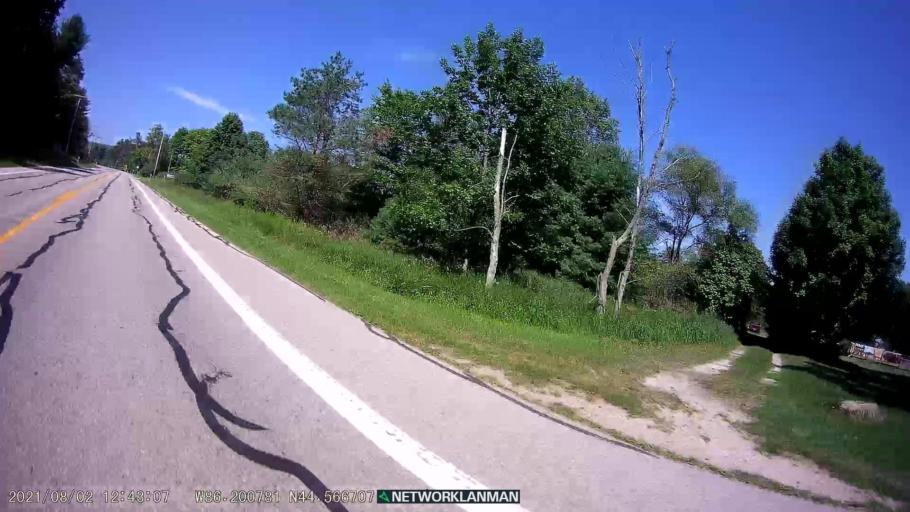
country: US
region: Michigan
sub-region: Benzie County
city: Frankfort
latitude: 44.5670
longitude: -86.2008
